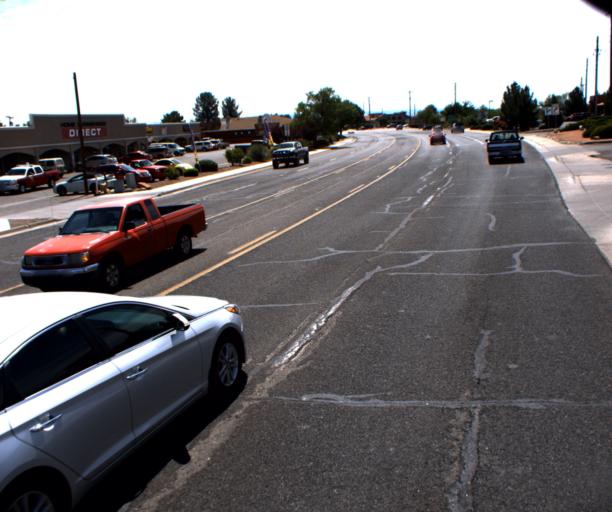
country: US
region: Arizona
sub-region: Yavapai County
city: Verde Village
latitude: 34.7229
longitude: -112.0049
